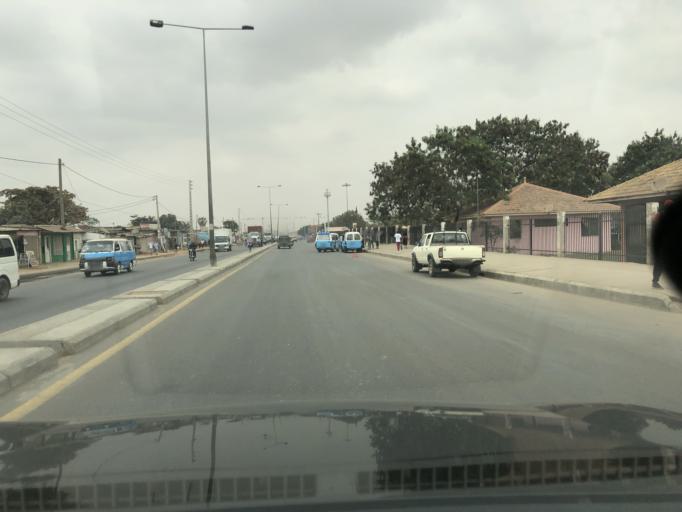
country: AO
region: Luanda
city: Luanda
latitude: -8.8285
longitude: 13.2827
